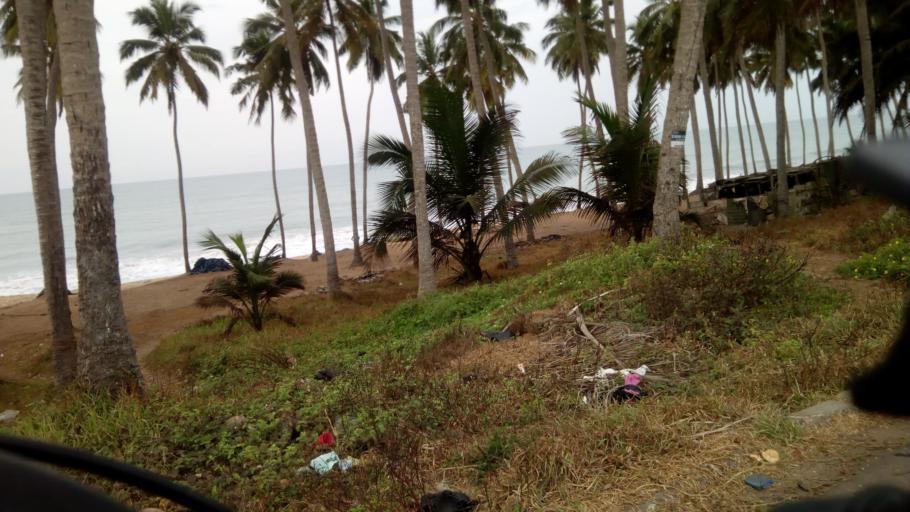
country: GH
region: Central
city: Cape Coast
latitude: 5.1008
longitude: -1.2784
